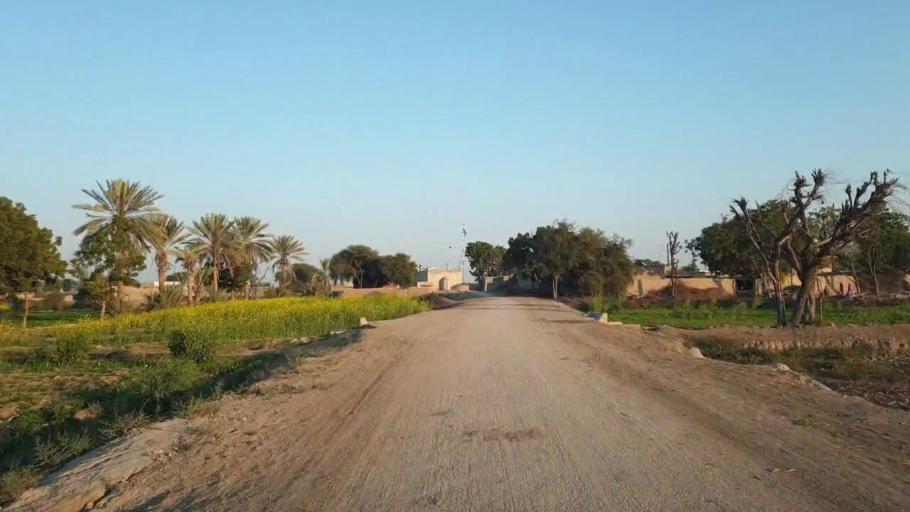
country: PK
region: Sindh
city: Shahpur Chakar
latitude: 26.1530
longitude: 68.5675
